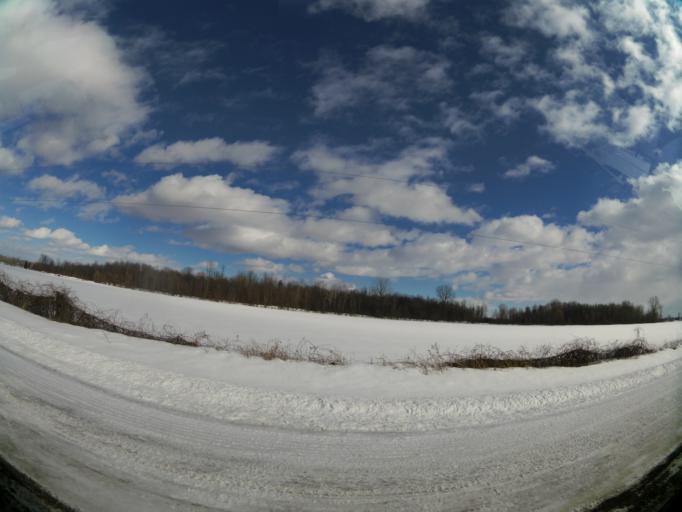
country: CA
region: Ontario
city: Ottawa
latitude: 45.3205
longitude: -75.5123
